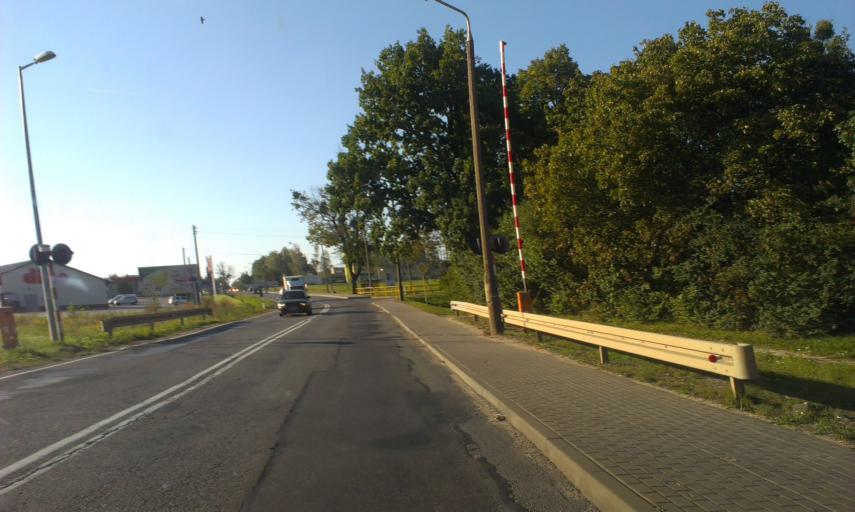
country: PL
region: Kujawsko-Pomorskie
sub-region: Powiat tucholski
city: Tuchola
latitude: 53.5780
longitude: 17.8782
